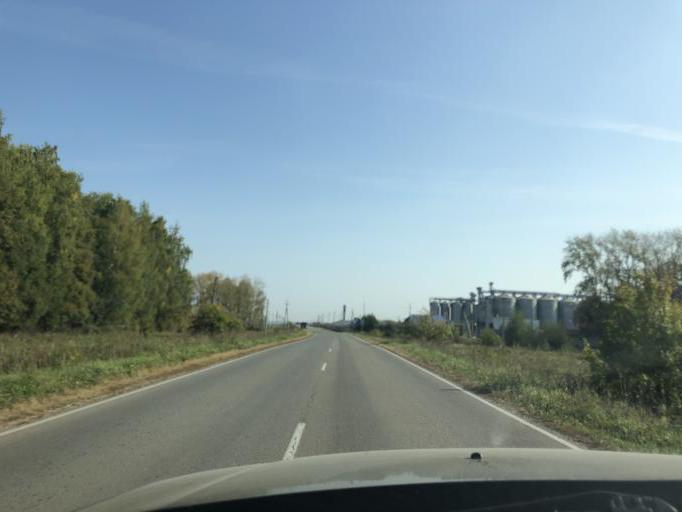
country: RU
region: Tula
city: Novogurovskiy
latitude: 54.4569
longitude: 37.4435
